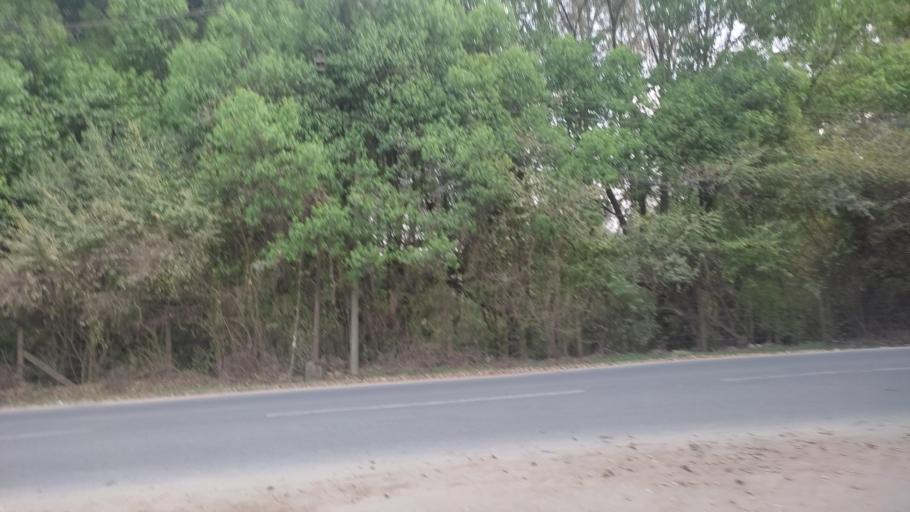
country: NP
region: Central Region
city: Kirtipur
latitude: 27.6798
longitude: 85.2921
